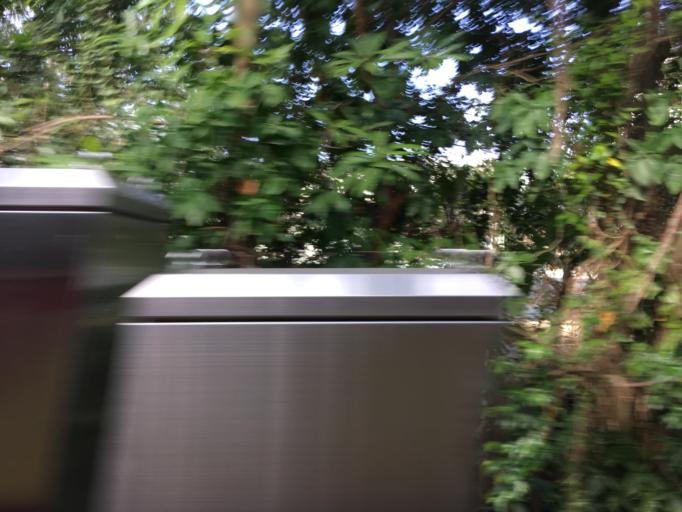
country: TW
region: Taiwan
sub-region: Chiayi
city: Jiayi Shi
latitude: 23.4944
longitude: 120.4970
